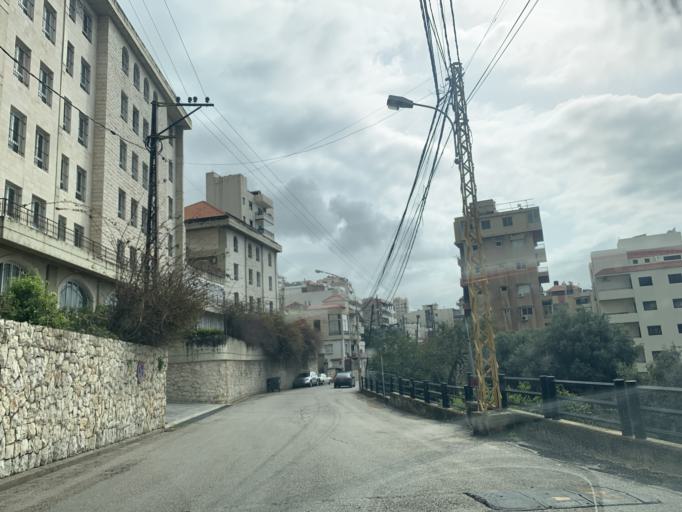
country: LB
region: Mont-Liban
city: Djounie
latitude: 33.9853
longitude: 35.6421
